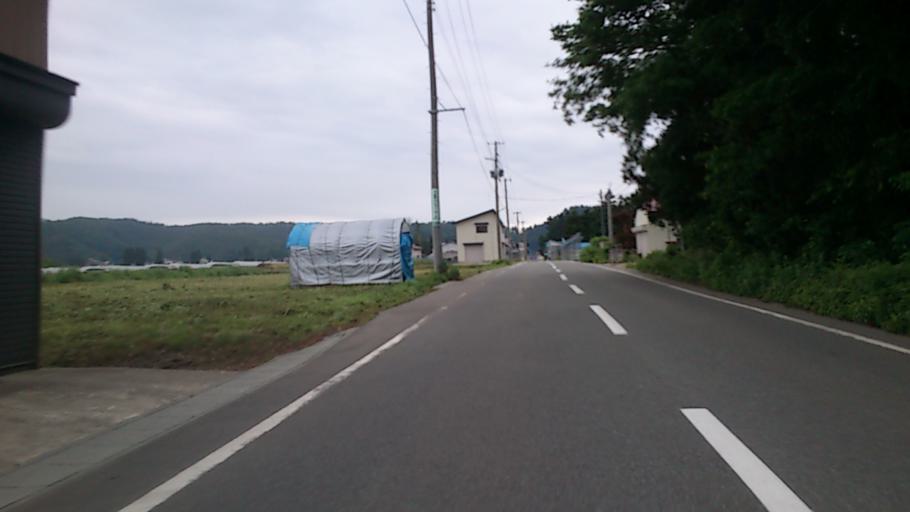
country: JP
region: Yamagata
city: Obanazawa
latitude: 38.5767
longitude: 140.4874
